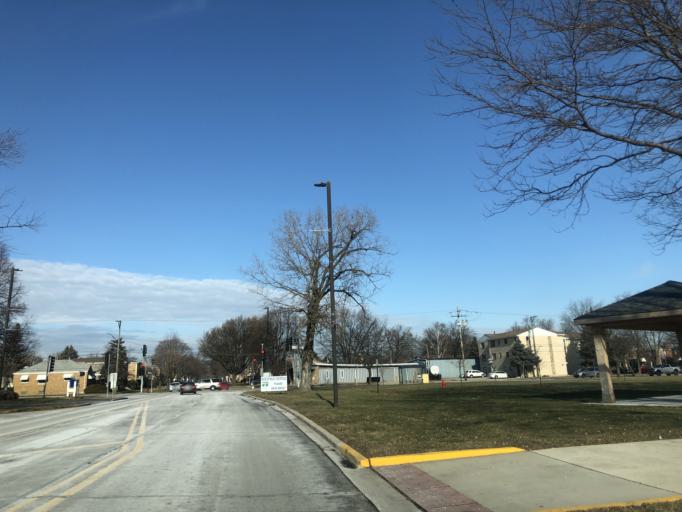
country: US
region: Illinois
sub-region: Cook County
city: Stickney
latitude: 41.8206
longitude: -87.7826
